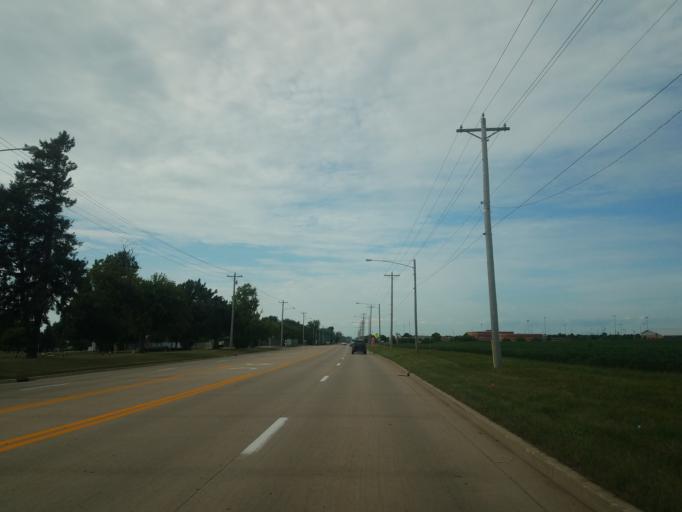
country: US
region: Illinois
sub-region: McLean County
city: Bloomington
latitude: 40.4895
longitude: -88.9238
